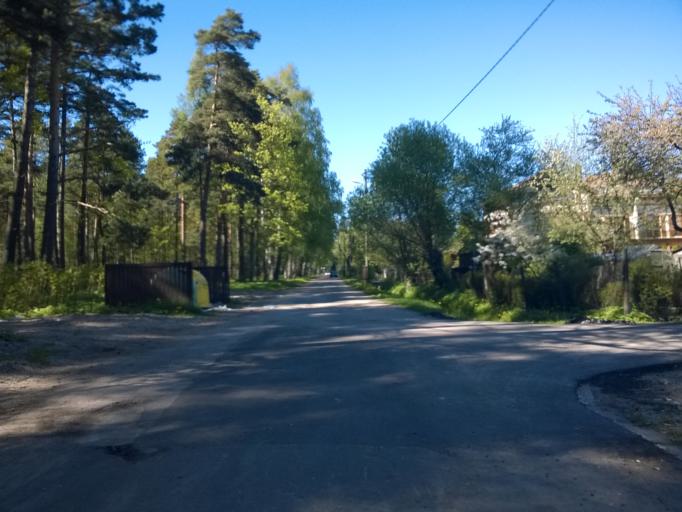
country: LV
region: Jurmala
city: Jurmala
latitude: 56.9559
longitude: 23.6667
